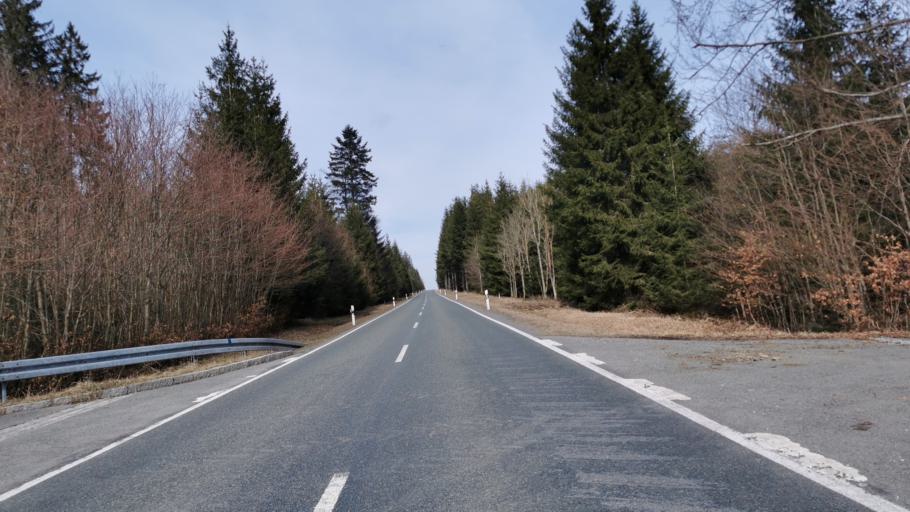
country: DE
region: Bavaria
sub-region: Upper Franconia
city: Tschirn
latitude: 50.4258
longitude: 11.4597
